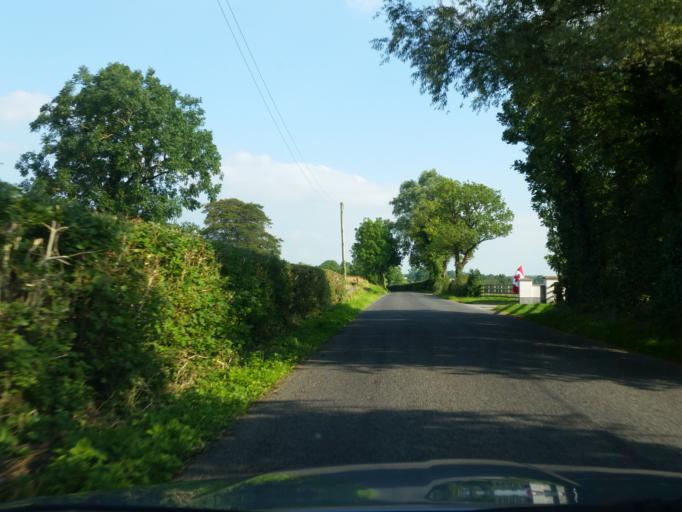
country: GB
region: Northern Ireland
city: Lisnaskea
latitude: 54.2892
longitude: -7.4600
